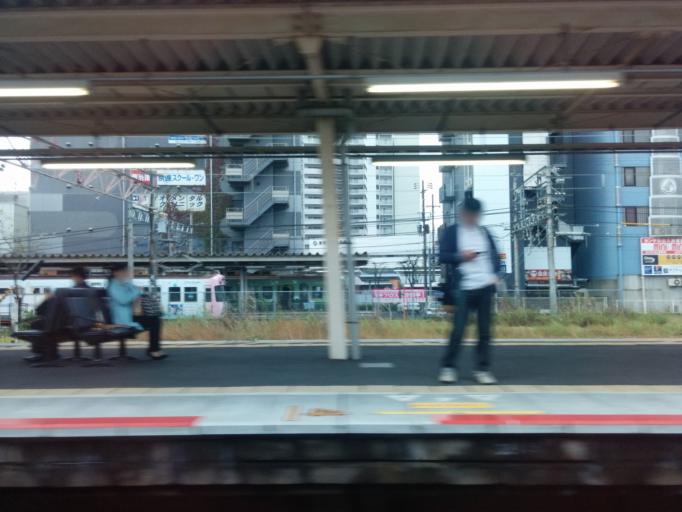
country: JP
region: Shiga Prefecture
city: Otsu-shi
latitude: 34.9800
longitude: 135.8992
